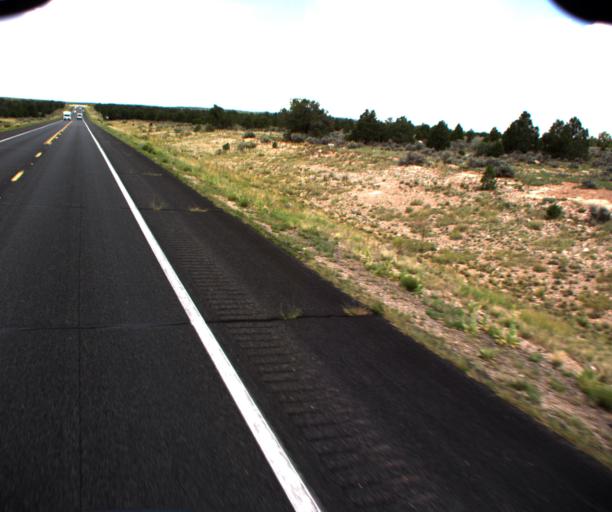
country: US
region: Arizona
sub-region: Coconino County
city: Grand Canyon
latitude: 35.9324
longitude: -111.7680
